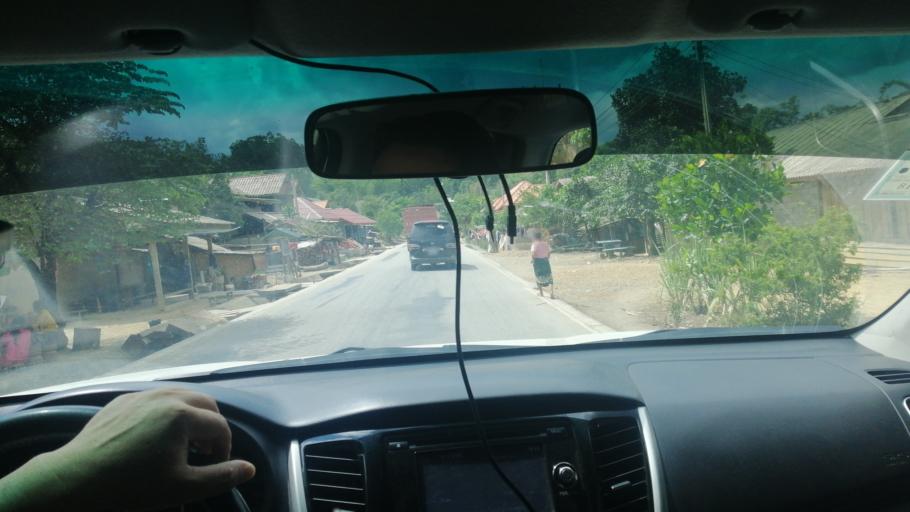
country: LA
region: Loungnamtha
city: Louang Namtha
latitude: 21.0372
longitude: 101.6502
